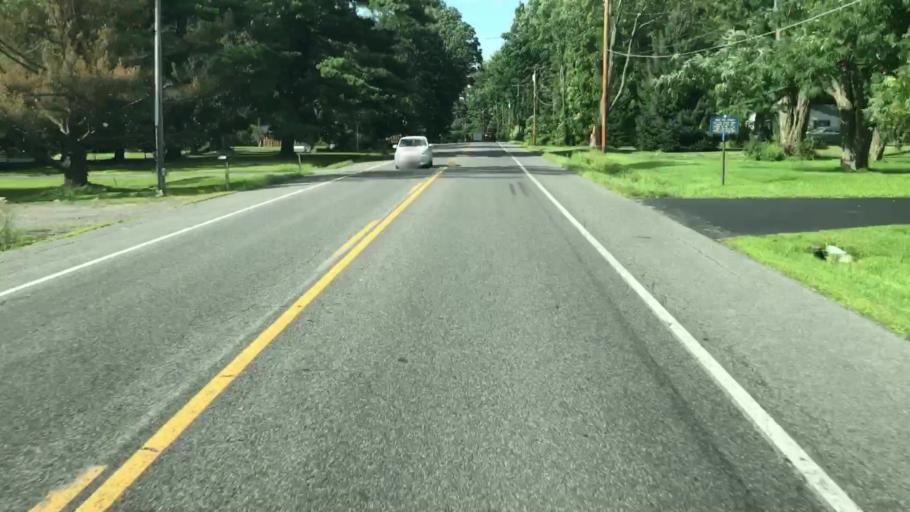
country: US
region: New York
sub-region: Onondaga County
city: Liverpool
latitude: 43.1613
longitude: -76.1947
